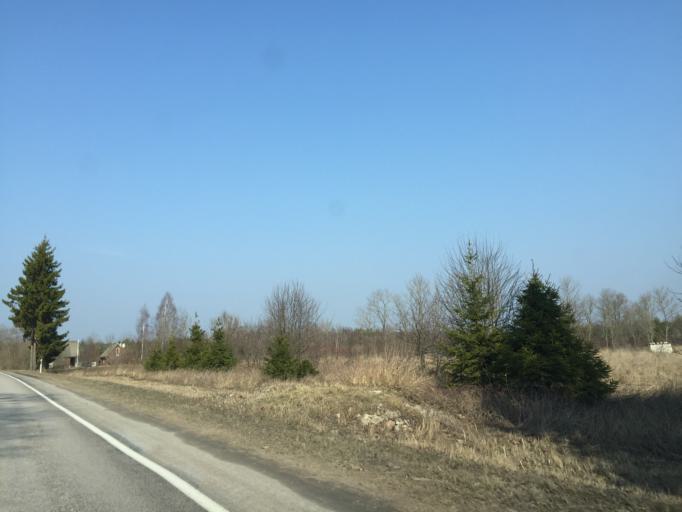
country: EE
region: Saare
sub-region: Kuressaare linn
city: Kuressaare
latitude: 58.2712
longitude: 22.4603
